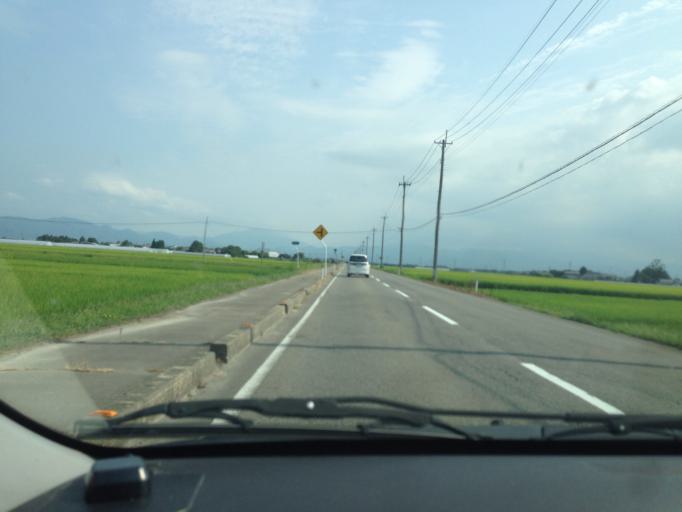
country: JP
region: Fukushima
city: Kitakata
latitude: 37.5464
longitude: 139.8561
